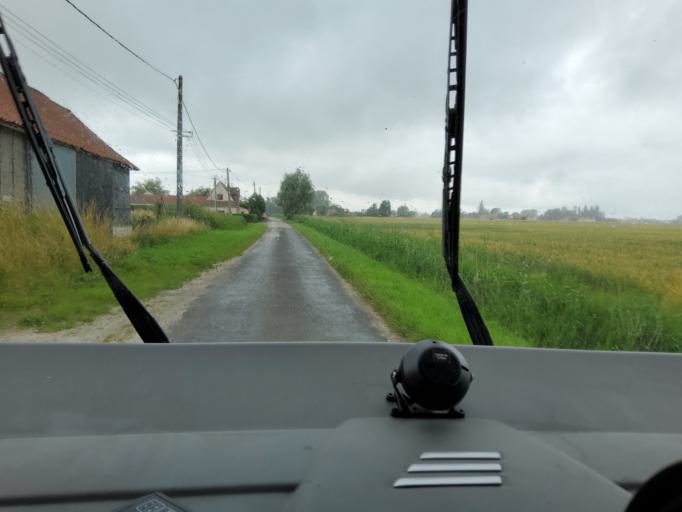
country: FR
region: Nord-Pas-de-Calais
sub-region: Departement du Pas-de-Calais
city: Sainte-Marie-Kerque
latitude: 50.9196
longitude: 2.1491
